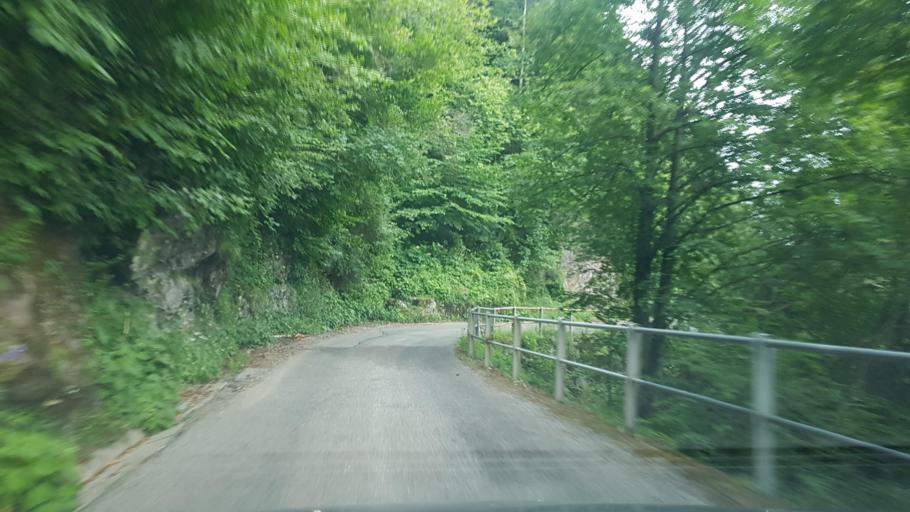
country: IT
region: Friuli Venezia Giulia
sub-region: Provincia di Udine
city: Paularo
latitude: 46.5534
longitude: 13.1224
